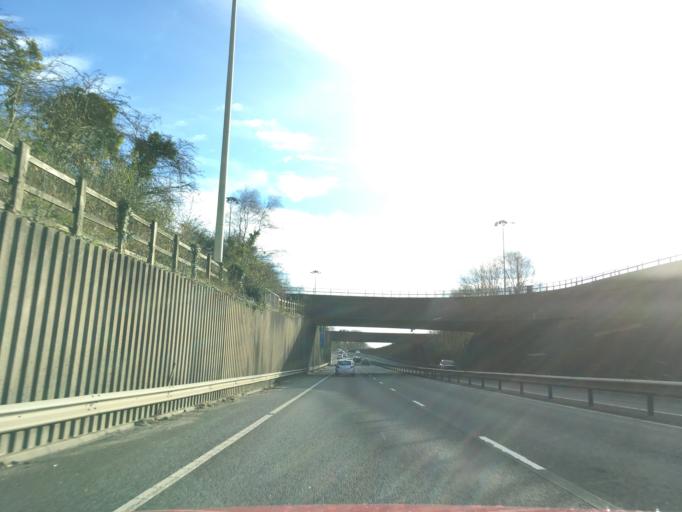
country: GB
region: Wales
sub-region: Cardiff
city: Radyr
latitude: 51.5374
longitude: -3.2598
